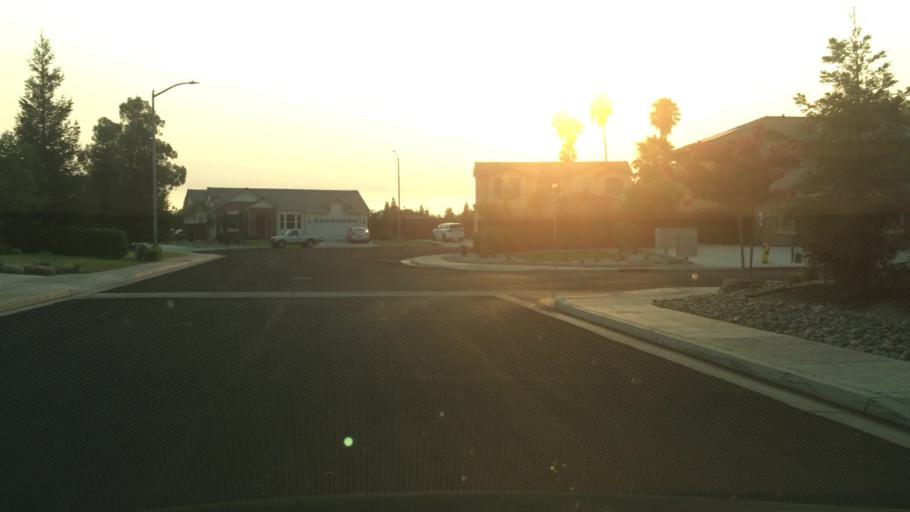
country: US
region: California
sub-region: Fresno County
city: Tarpey Village
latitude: 36.7929
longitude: -119.6771
